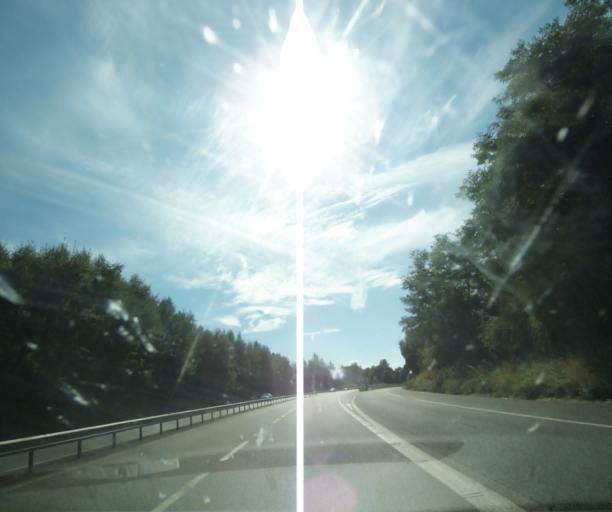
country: FR
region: Limousin
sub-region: Departement de la Correze
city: Donzenac
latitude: 45.2537
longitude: 1.5416
